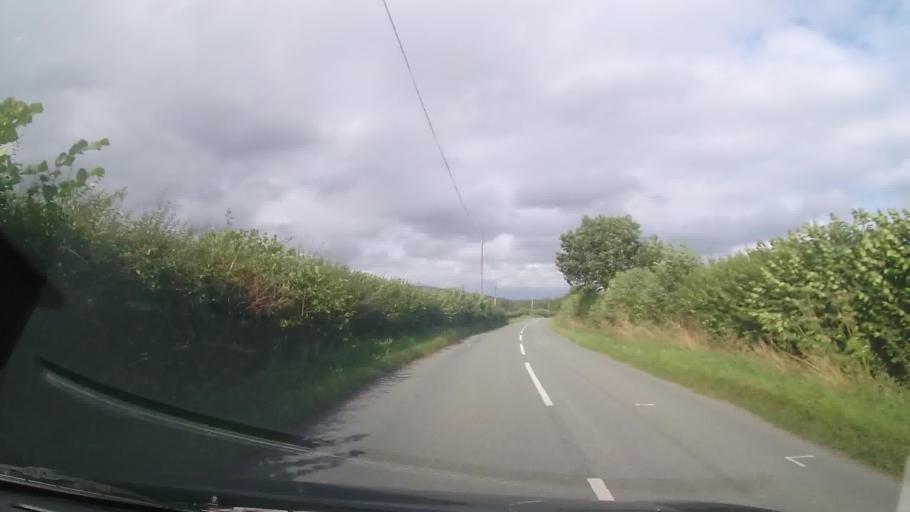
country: GB
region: England
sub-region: Shropshire
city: Lydham
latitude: 52.5157
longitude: -2.9636
